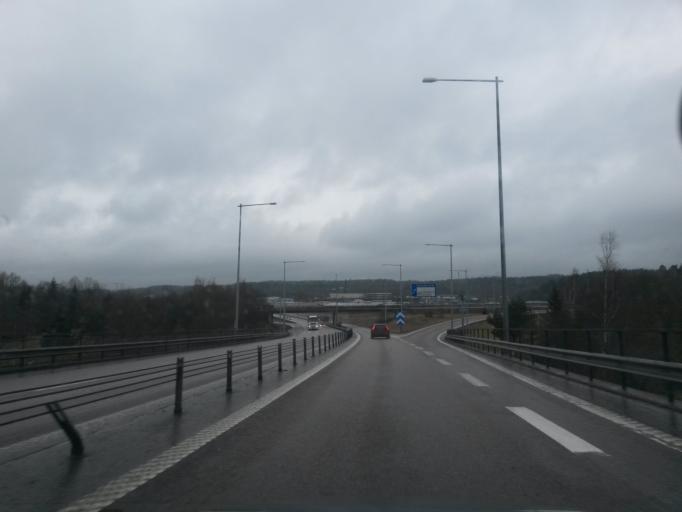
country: SE
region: Vaestra Goetaland
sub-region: Uddevalla Kommun
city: Uddevalla
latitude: 58.3475
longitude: 11.9860
